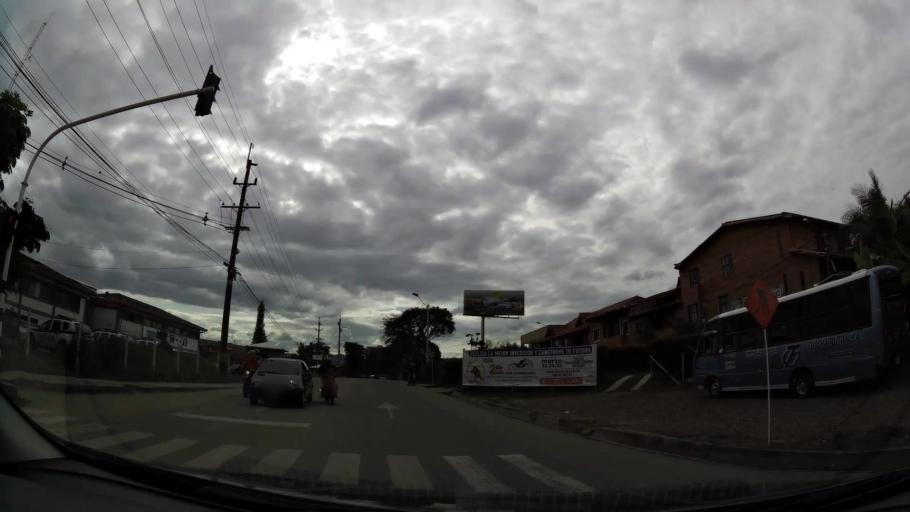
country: CO
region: Antioquia
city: Rionegro
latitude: 6.1507
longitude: -75.3901
